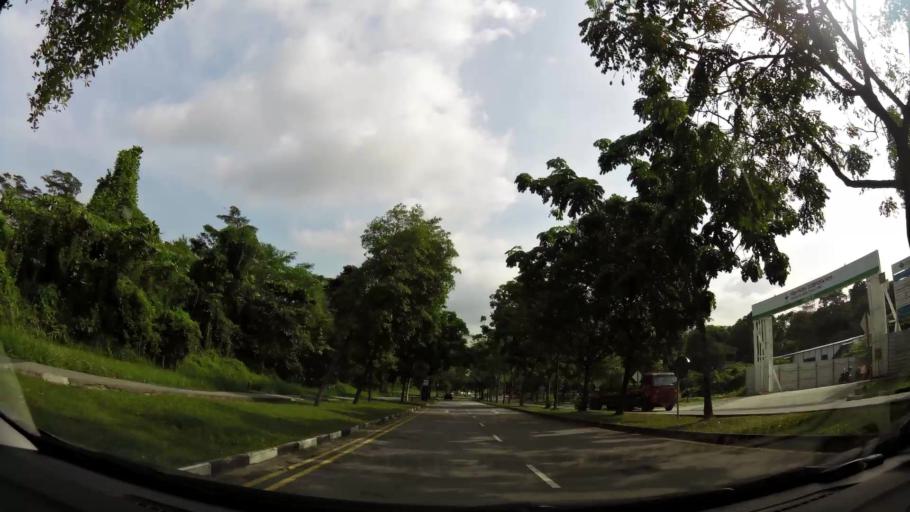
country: SG
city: Singapore
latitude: 1.2990
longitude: 103.7913
